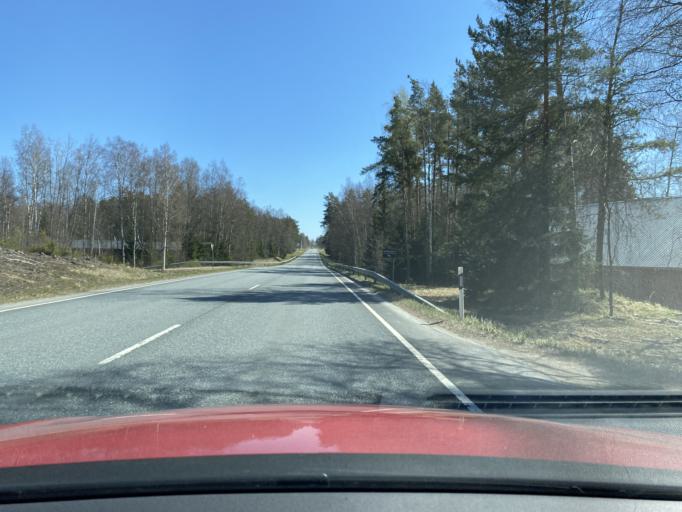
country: FI
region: Haeme
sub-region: Forssa
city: Humppila
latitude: 60.9714
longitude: 23.2723
